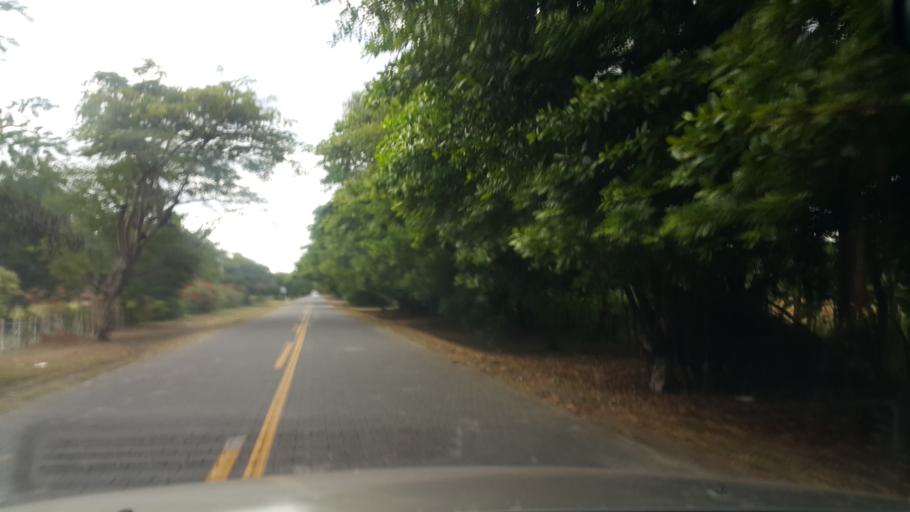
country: NI
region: Rivas
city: Moyogalpa
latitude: 11.4947
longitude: -85.6833
